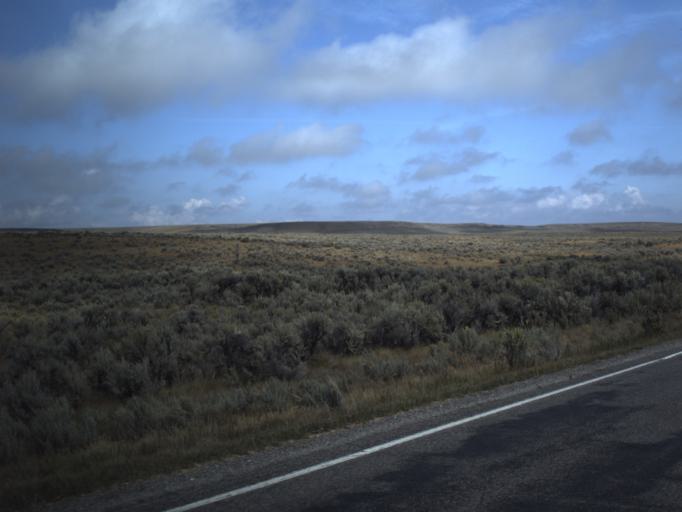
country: US
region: Utah
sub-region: Rich County
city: Randolph
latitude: 41.7475
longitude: -111.1474
